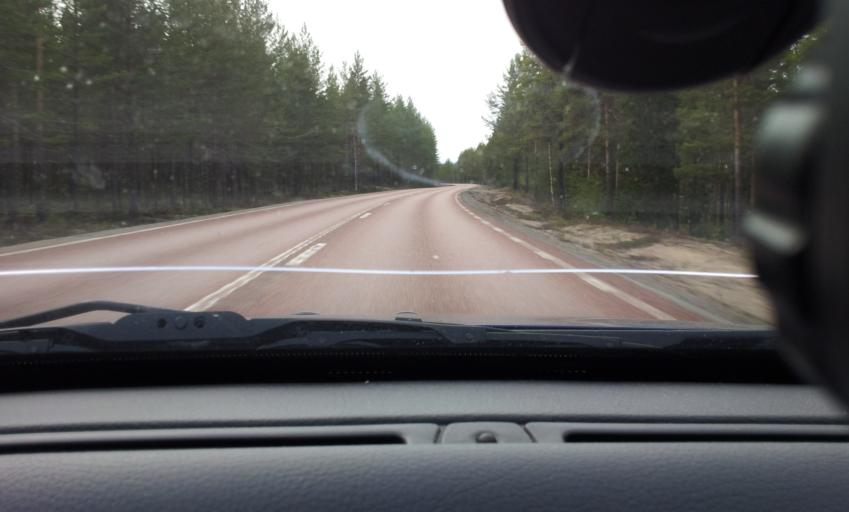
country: SE
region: Gaevleborg
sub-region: Ljusdals Kommun
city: Farila
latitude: 61.9016
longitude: 15.6414
